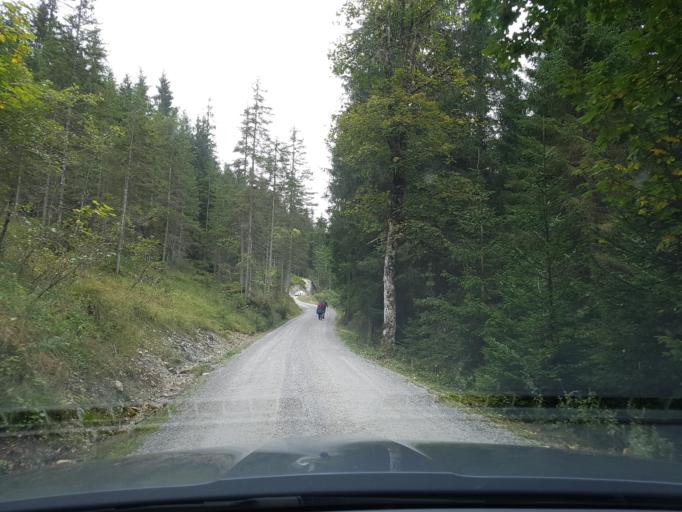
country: AT
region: Salzburg
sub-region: Politischer Bezirk Sankt Johann im Pongau
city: Forstau
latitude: 47.3401
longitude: 13.5775
